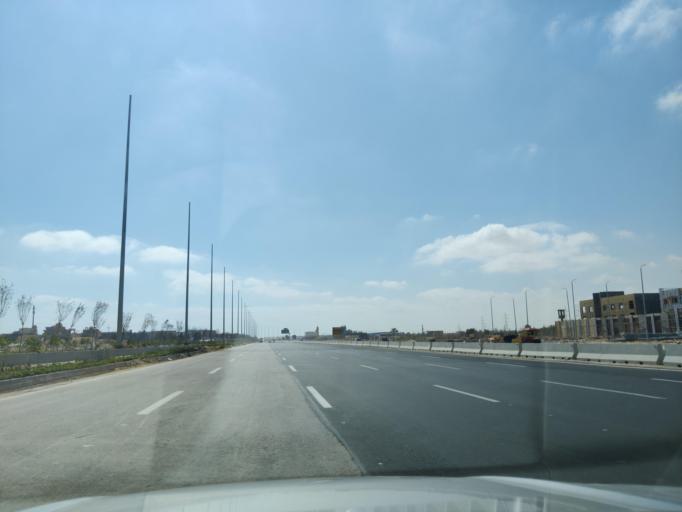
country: EG
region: Muhafazat Matruh
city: Al `Alamayn
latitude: 30.9900
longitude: 28.6849
